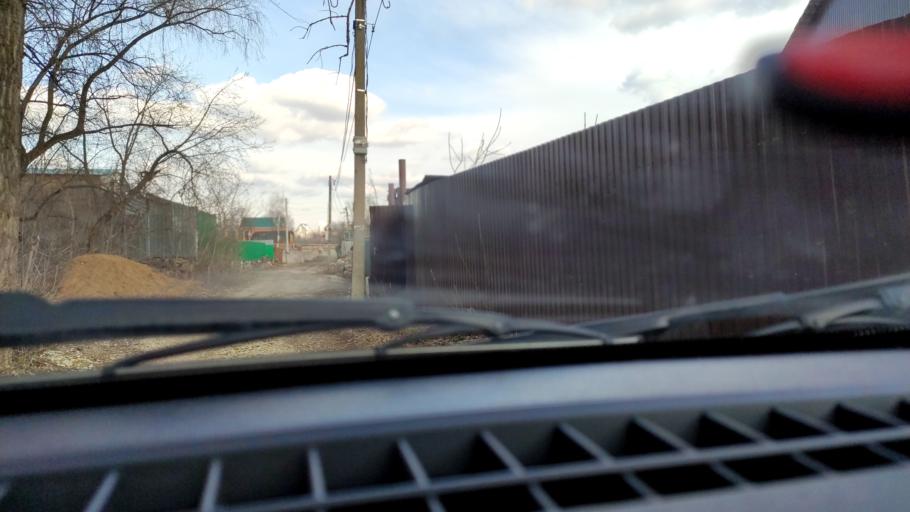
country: RU
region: Bashkortostan
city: Ufa
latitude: 54.7075
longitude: 55.9350
